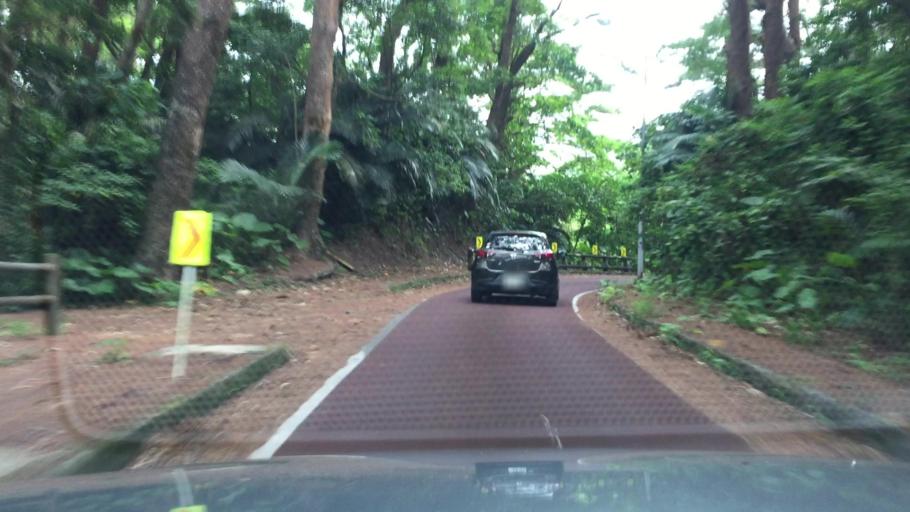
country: JP
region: Okinawa
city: Ishigaki
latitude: 24.4507
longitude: 124.1360
